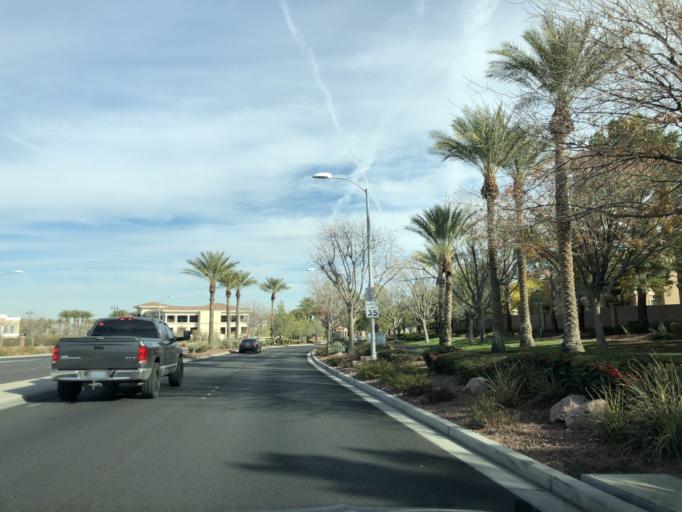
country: US
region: Nevada
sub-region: Clark County
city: Whitney
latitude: 36.0192
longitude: -115.0867
